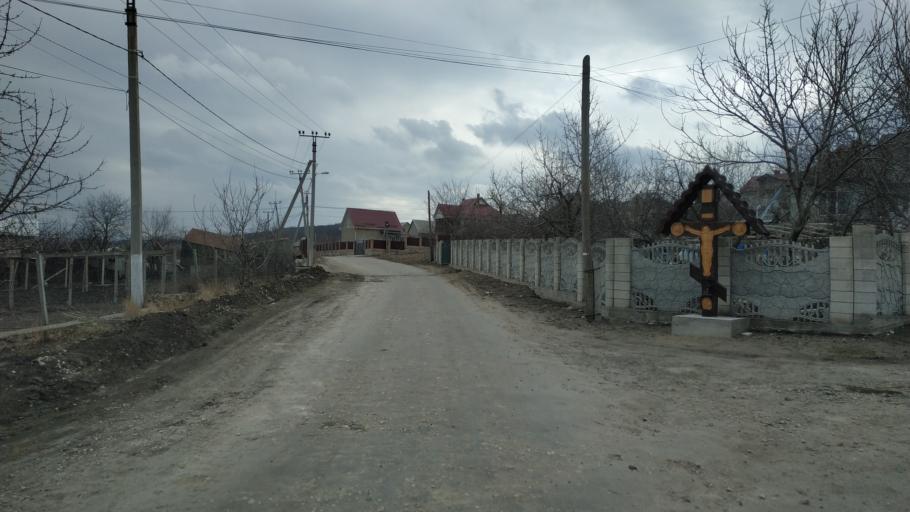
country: MD
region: Laloveni
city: Ialoveni
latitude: 46.8563
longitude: 28.7864
